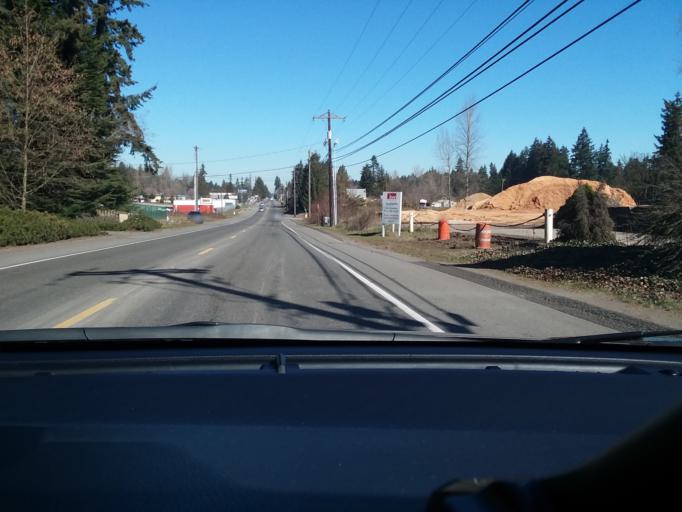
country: US
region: Washington
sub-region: Pierce County
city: Summit
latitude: 47.1723
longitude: -122.3571
